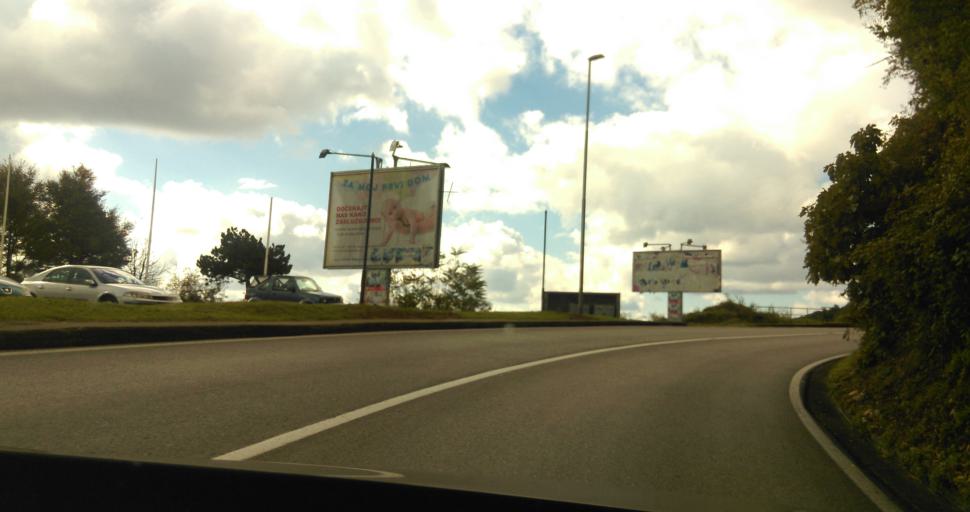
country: ME
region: Budva
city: Budva
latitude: 42.2782
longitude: 18.8334
